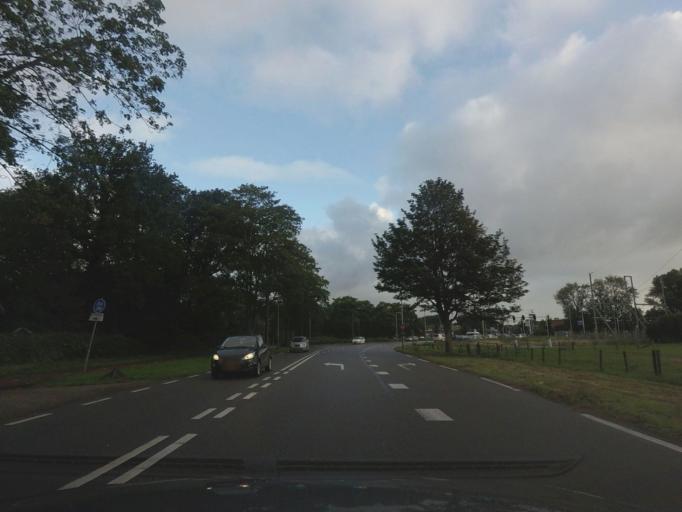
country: NL
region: North Holland
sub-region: Gemeente Velsen
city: Velsen-Zuid
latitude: 52.4572
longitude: 4.6501
